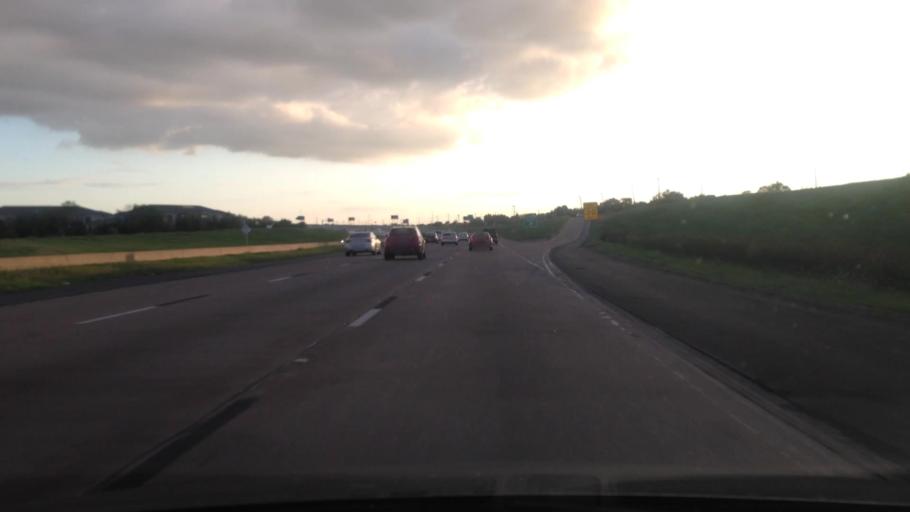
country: US
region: Texas
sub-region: Tarrant County
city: White Settlement
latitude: 32.7831
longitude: -97.4677
